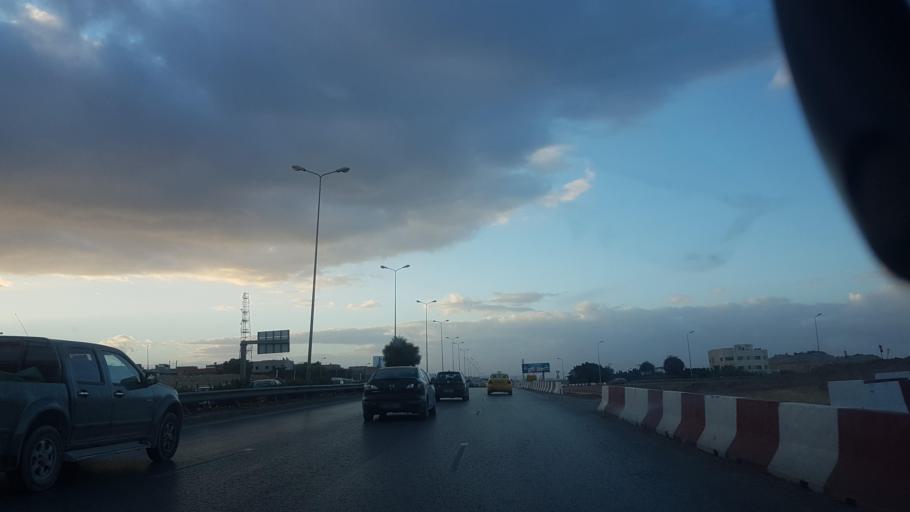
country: TN
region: Bin 'Arus
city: Ben Arous
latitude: 36.7469
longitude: 10.2094
